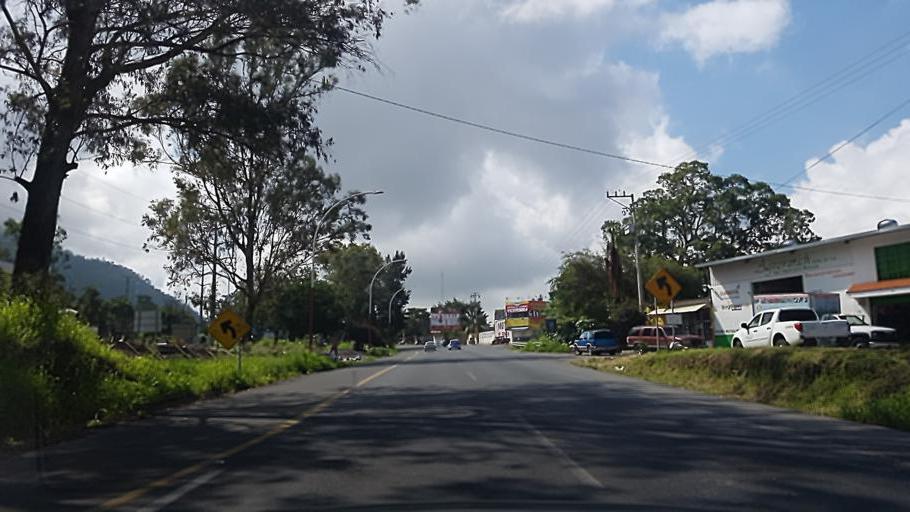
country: MX
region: Nayarit
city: Tepic
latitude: 21.4986
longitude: -104.9092
